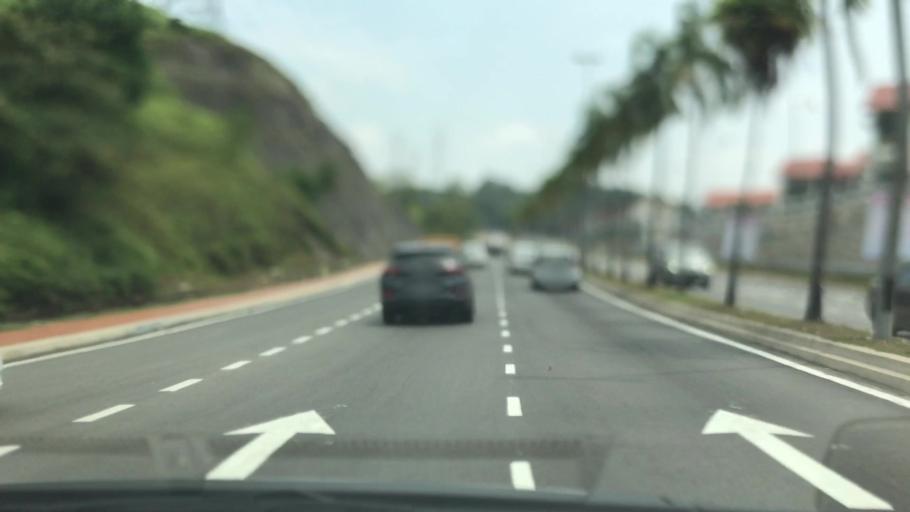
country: MY
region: Selangor
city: Kampong Baharu Balakong
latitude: 3.0367
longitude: 101.6768
